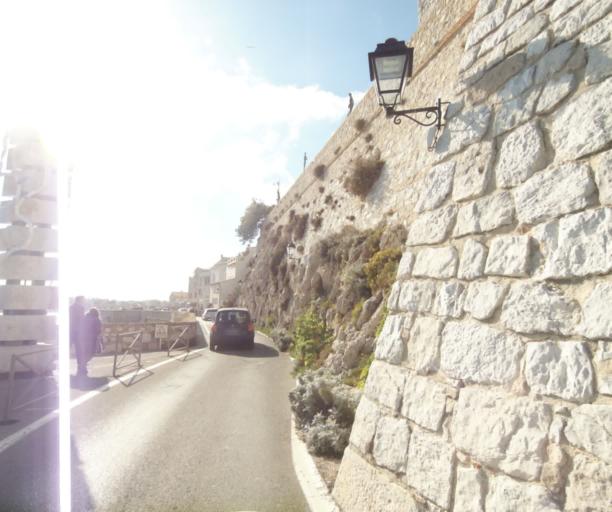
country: FR
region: Provence-Alpes-Cote d'Azur
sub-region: Departement des Alpes-Maritimes
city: Antibes
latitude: 43.5808
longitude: 7.1286
